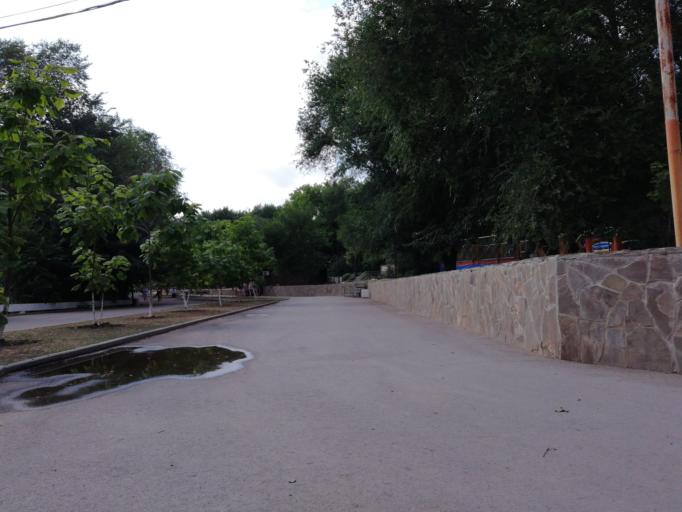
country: RU
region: Rostov
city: Severnyy
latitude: 47.2770
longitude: 39.7151
